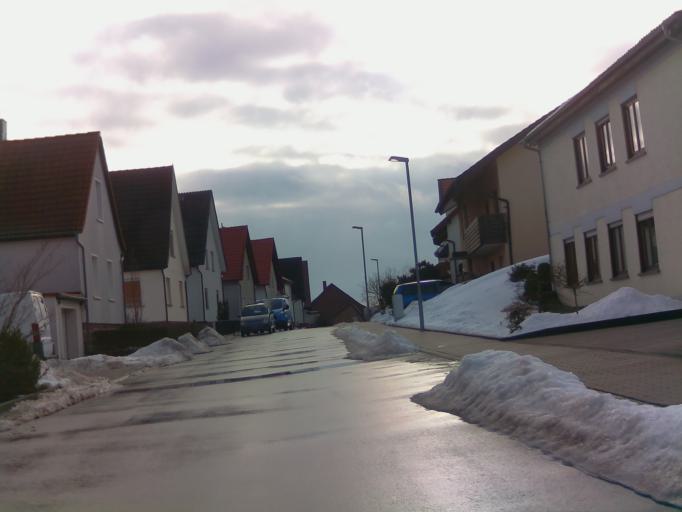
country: DE
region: Baden-Wuerttemberg
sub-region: Karlsruhe Region
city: Mudau
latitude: 49.5368
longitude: 9.1980
